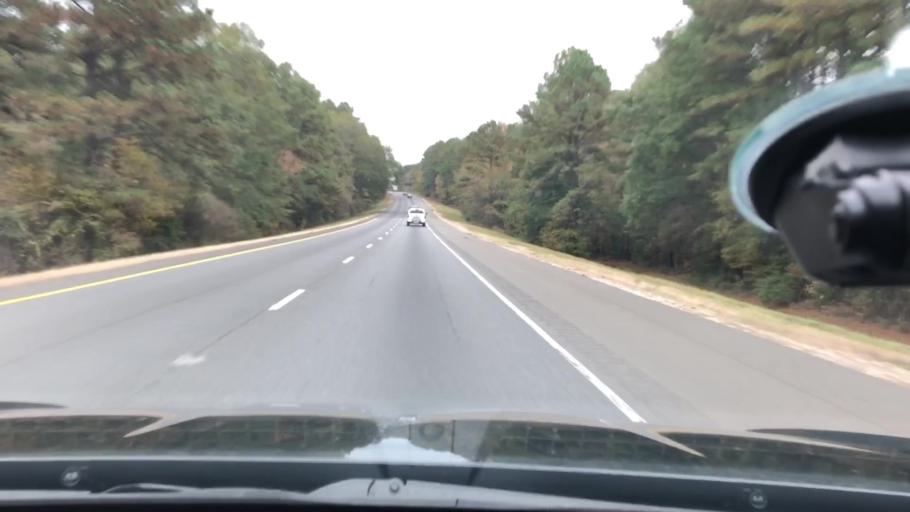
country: US
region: Arkansas
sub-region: Hot Spring County
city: Malvern
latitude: 34.3056
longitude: -92.9418
